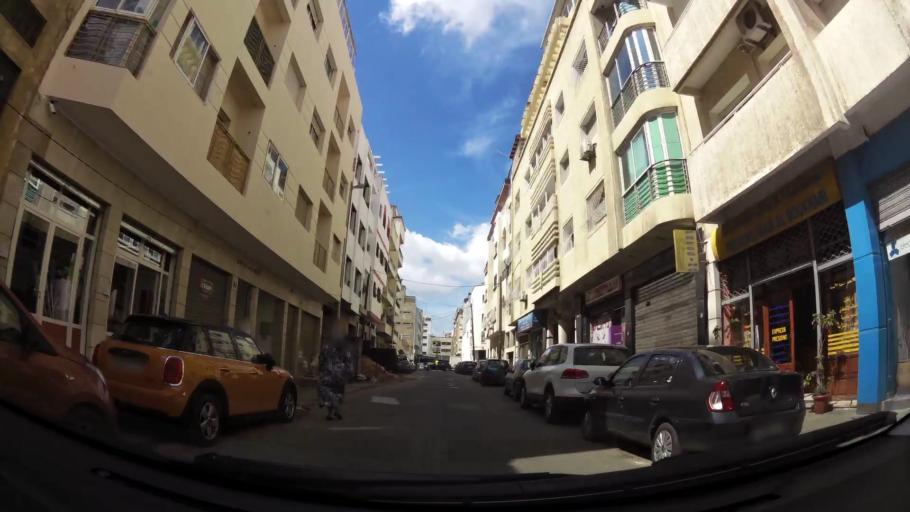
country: MA
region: Grand Casablanca
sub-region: Casablanca
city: Casablanca
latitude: 33.5778
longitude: -7.6415
